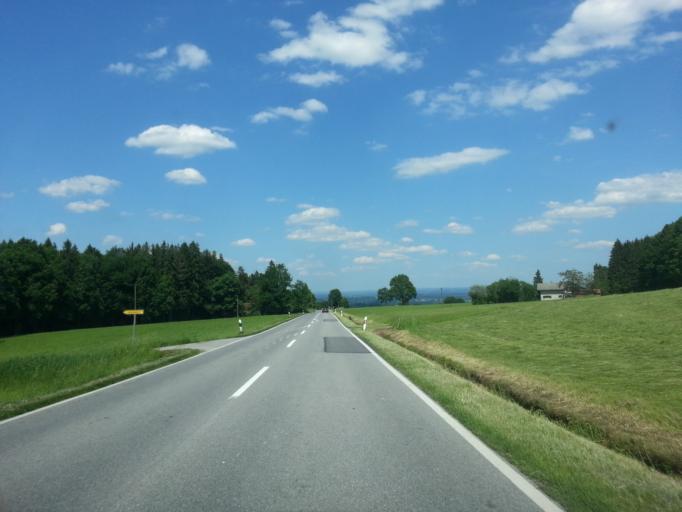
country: DE
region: Bavaria
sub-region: Upper Bavaria
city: Irschenberg
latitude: 47.8069
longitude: 11.9308
